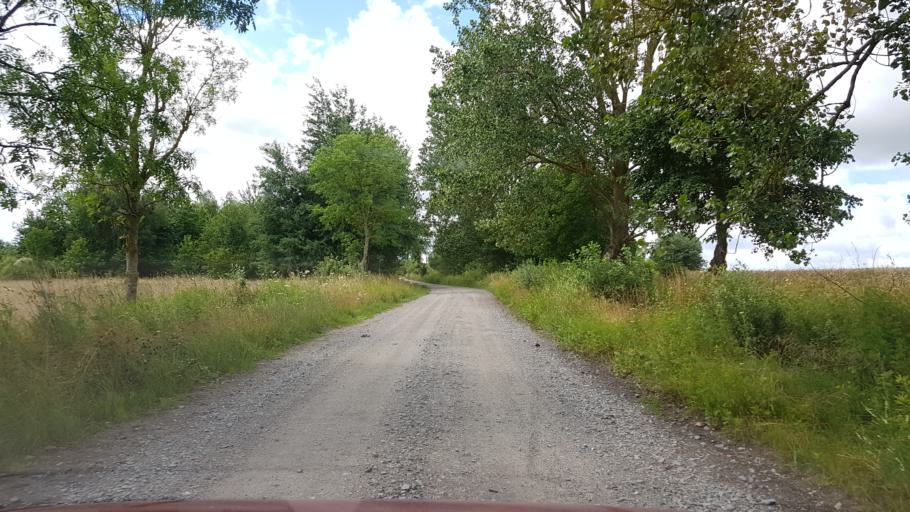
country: PL
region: West Pomeranian Voivodeship
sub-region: Powiat koszalinski
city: Mielno
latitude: 54.1678
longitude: 15.9560
